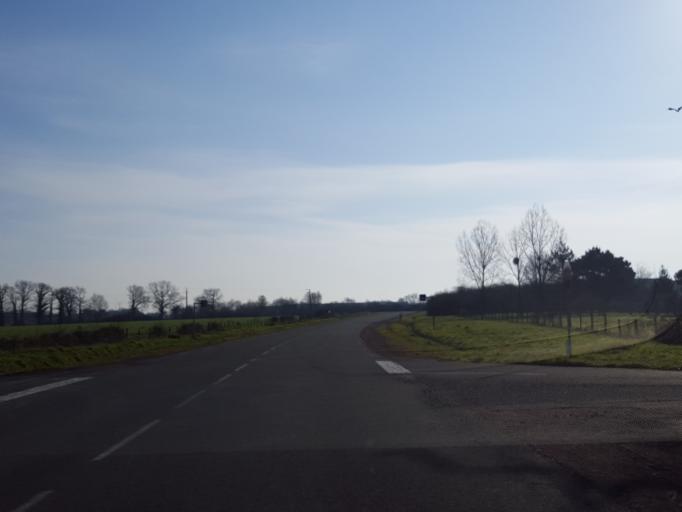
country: FR
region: Pays de la Loire
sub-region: Departement de la Vendee
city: La Chaize-le-Vicomte
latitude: 46.6694
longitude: -1.3322
